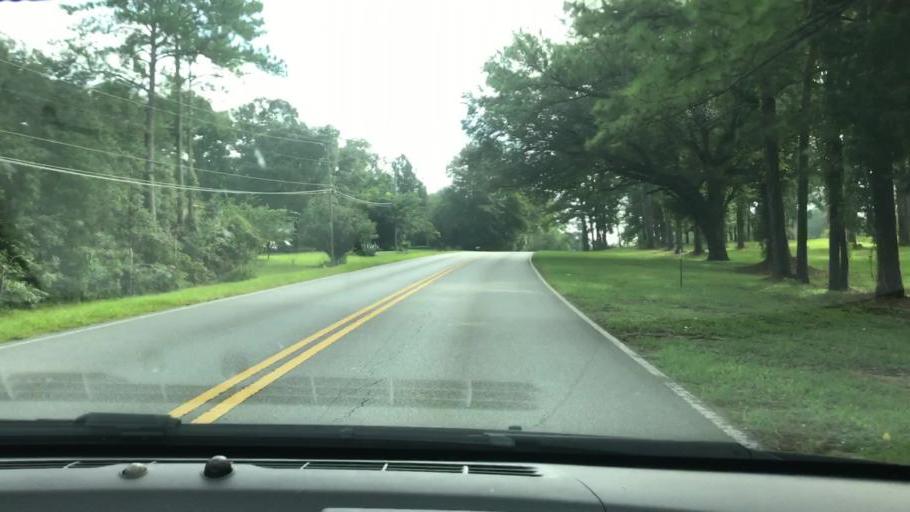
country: US
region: Florida
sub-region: Jackson County
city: Marianna
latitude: 30.7691
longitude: -85.2452
